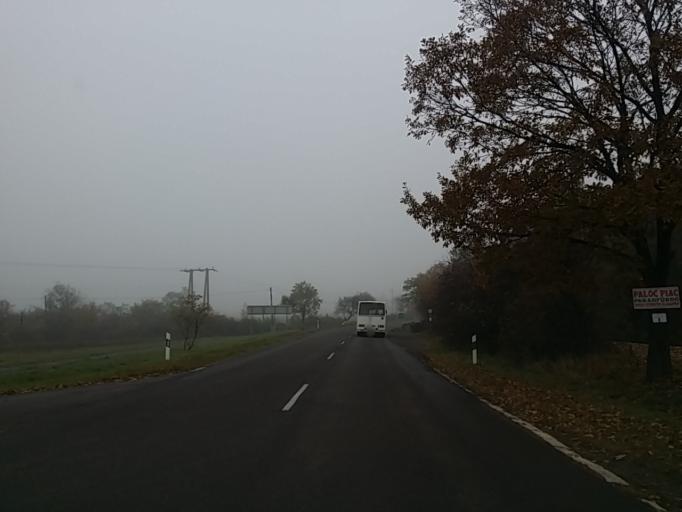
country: HU
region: Heves
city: Gyongyossolymos
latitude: 47.8161
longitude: 19.9592
